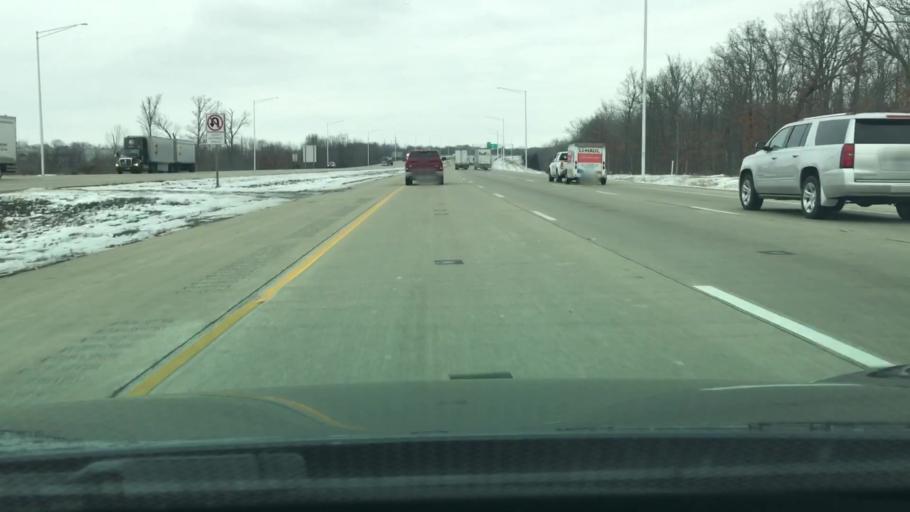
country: US
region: Illinois
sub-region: Jefferson County
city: Mount Vernon
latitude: 38.3203
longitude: -88.9545
